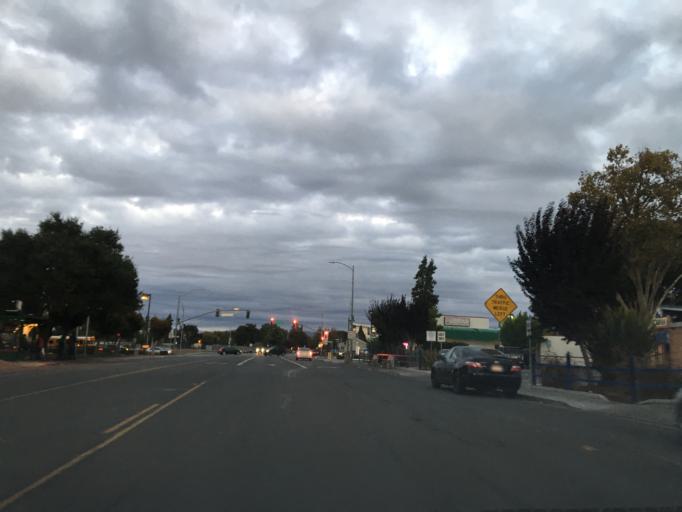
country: US
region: California
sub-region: San Mateo County
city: East Palo Alto
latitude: 37.4715
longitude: -122.1407
